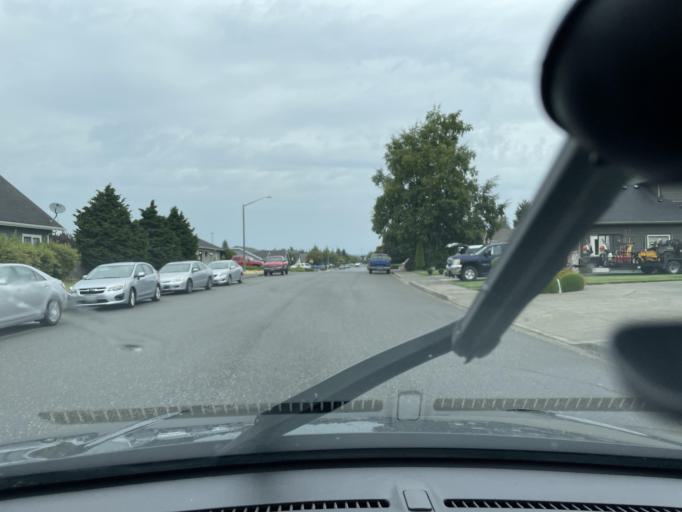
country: US
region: Washington
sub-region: Whatcom County
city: Lynden
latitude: 48.9573
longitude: -122.4253
